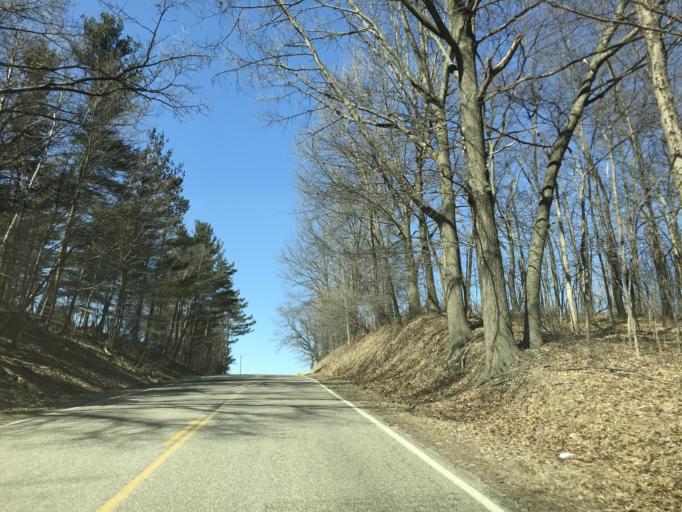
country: US
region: Michigan
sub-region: Hillsdale County
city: Litchfield
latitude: 41.9856
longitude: -84.7547
